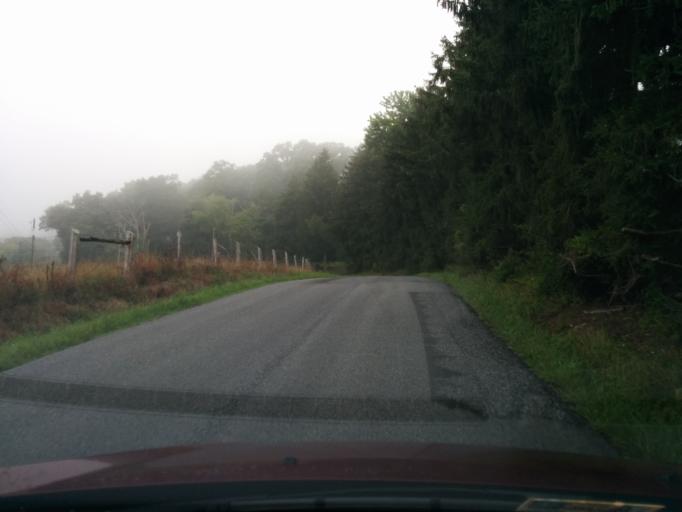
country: US
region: Virginia
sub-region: City of Lexington
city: Lexington
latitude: 37.7886
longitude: -79.4702
